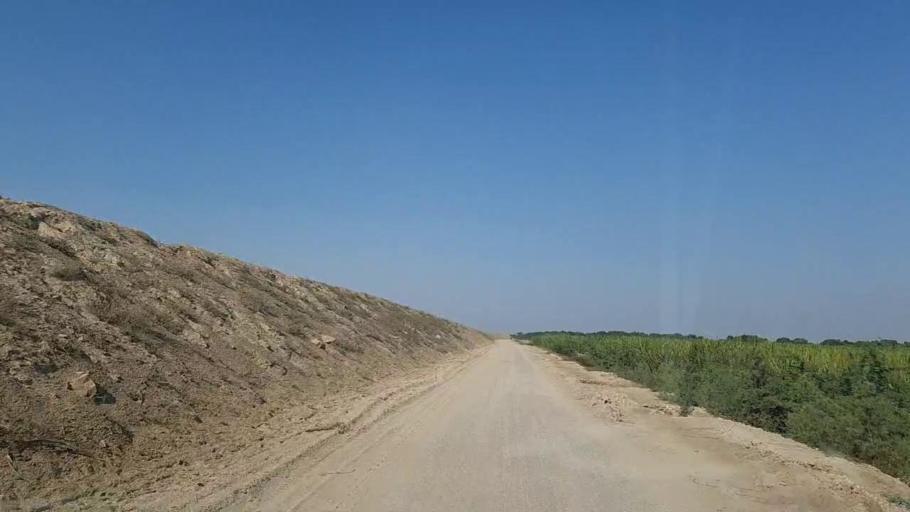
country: PK
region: Sindh
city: Chuhar Jamali
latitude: 24.5646
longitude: 68.0290
